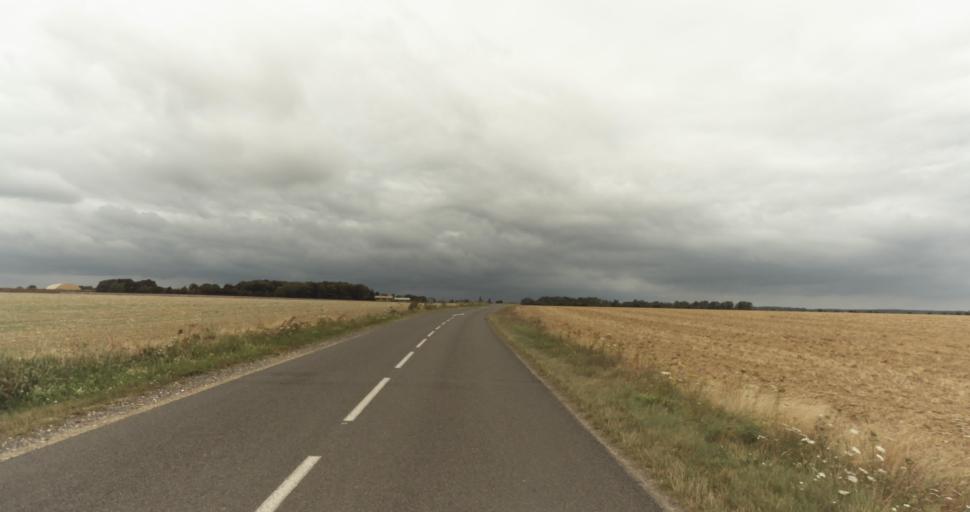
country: FR
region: Haute-Normandie
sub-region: Departement de l'Eure
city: Gravigny
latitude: 49.0414
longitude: 1.2360
